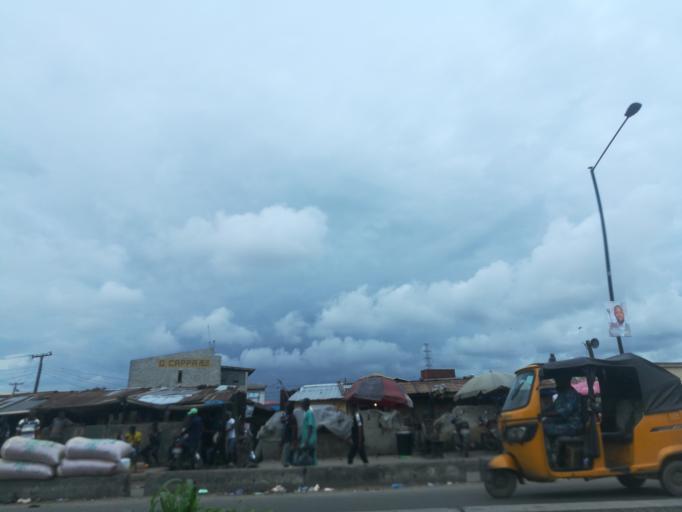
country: NG
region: Lagos
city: Ebute Metta
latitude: 6.4717
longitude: 3.3825
